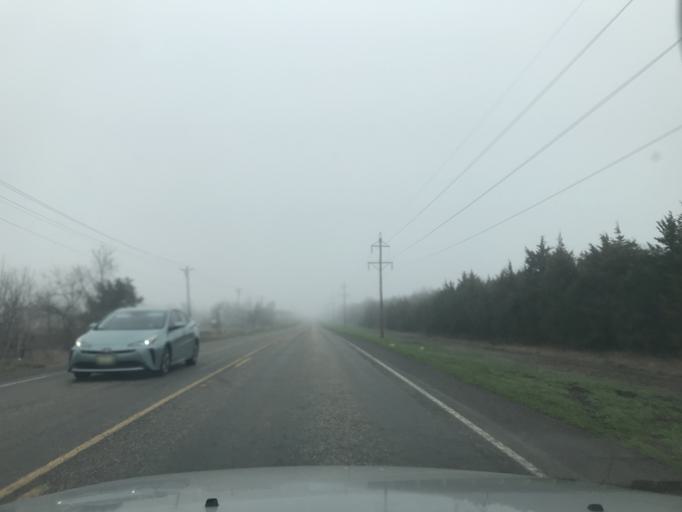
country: US
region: Texas
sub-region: Hunt County
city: Caddo Mills
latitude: 33.0264
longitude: -96.2719
